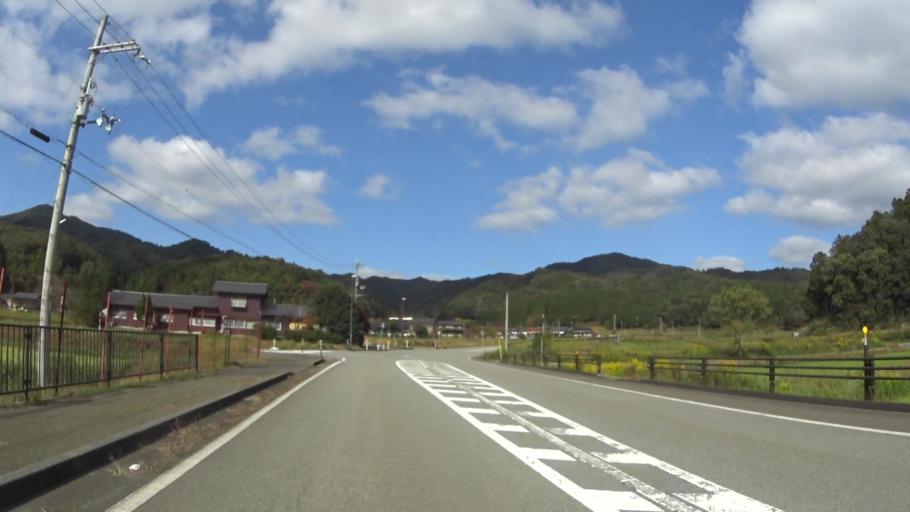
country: JP
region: Hyogo
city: Toyooka
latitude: 35.5057
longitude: 134.9918
